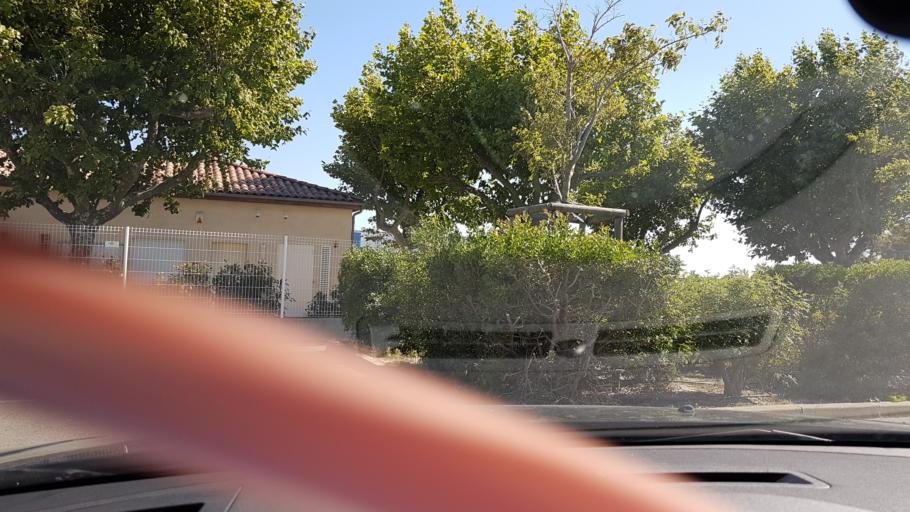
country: FR
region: Provence-Alpes-Cote d'Azur
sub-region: Departement des Bouches-du-Rhone
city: Port-Saint-Louis-du-Rhone
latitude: 43.3880
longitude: 4.8341
